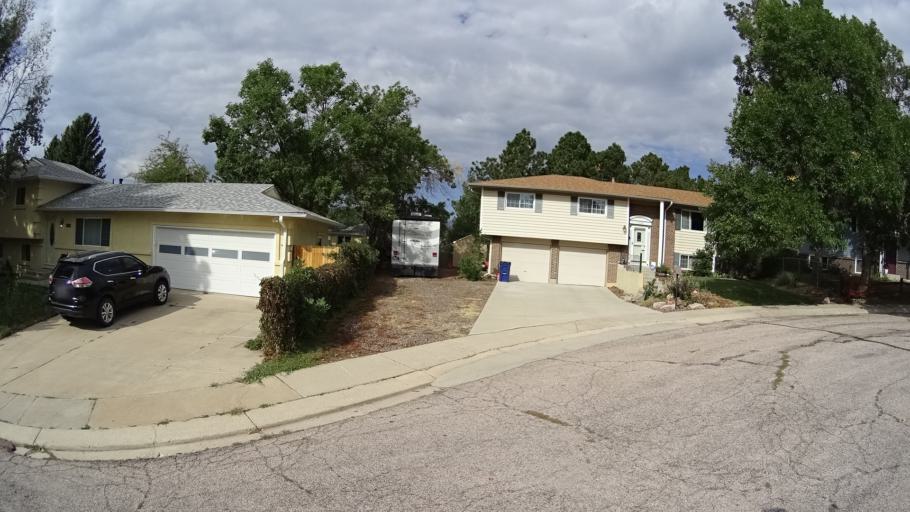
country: US
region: Colorado
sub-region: El Paso County
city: Cimarron Hills
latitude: 38.8558
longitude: -104.7401
